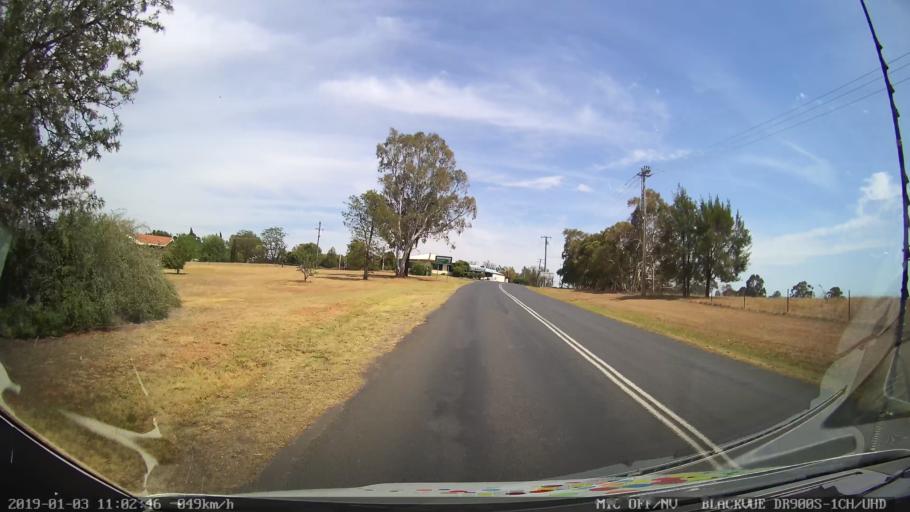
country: AU
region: New South Wales
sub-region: Young
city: Young
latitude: -34.2956
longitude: 148.2978
